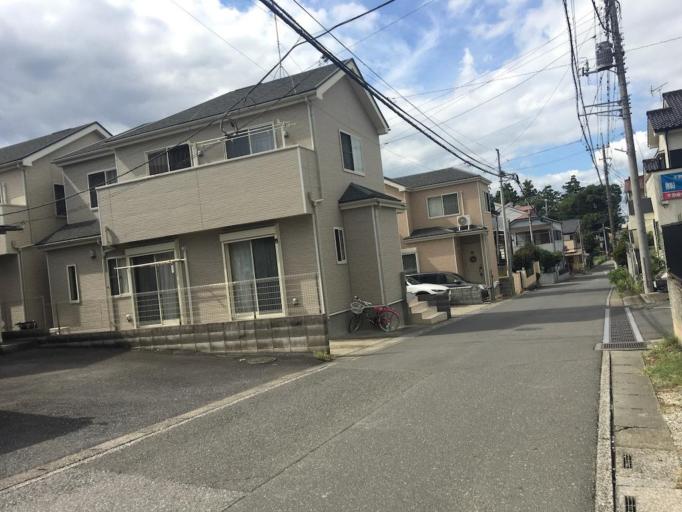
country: JP
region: Saitama
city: Kamifukuoka
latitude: 35.8915
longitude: 139.5024
